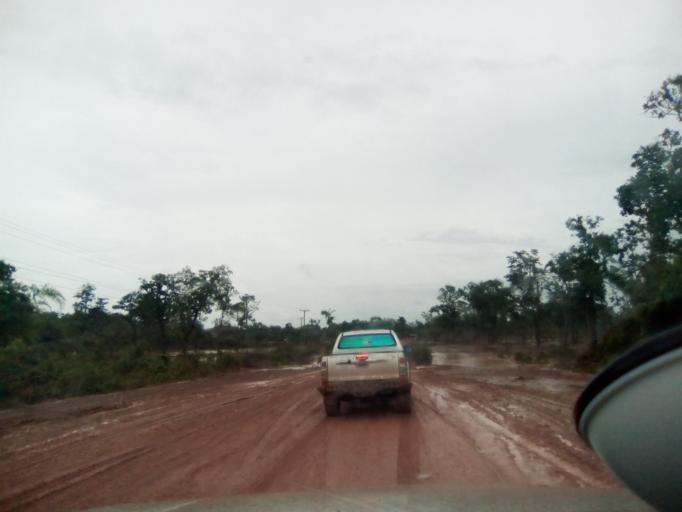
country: LA
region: Attapu
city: Attapu
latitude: 14.6925
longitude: 106.5364
